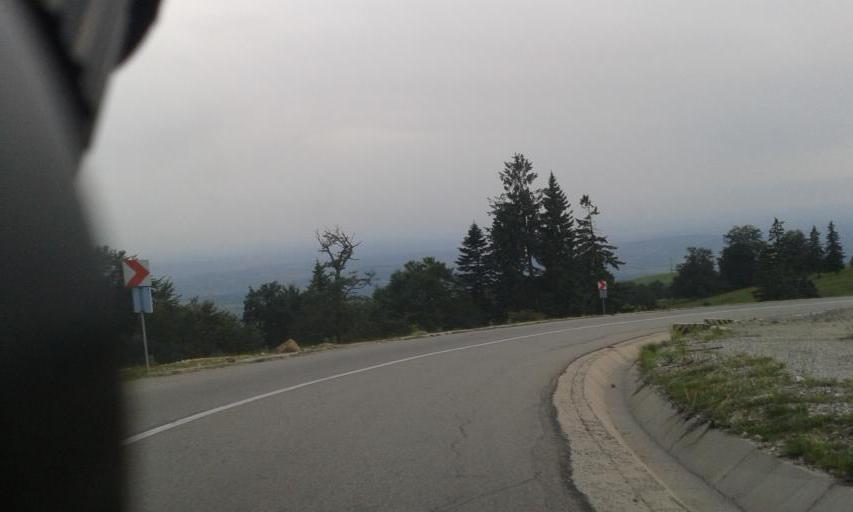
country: RO
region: Gorj
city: Novaci-Straini
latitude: 45.2395
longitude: 23.6966
